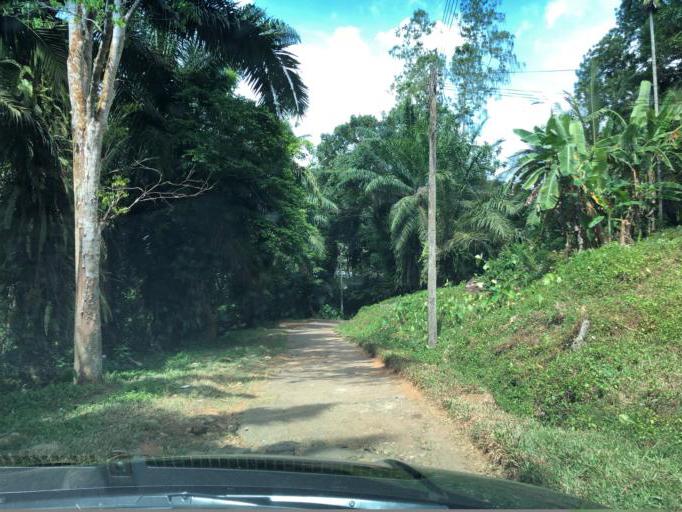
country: LK
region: Western
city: Horawala Junction
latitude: 6.5480
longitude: 80.0913
